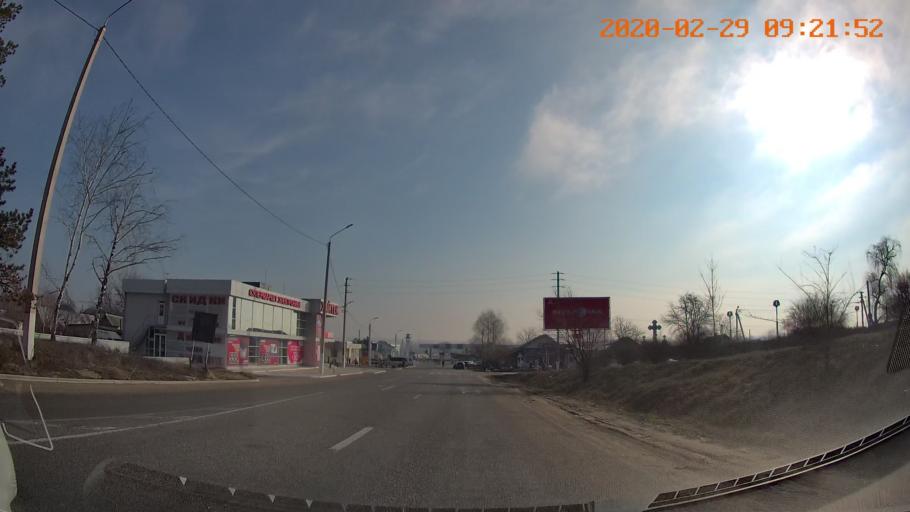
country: MD
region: Telenesti
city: Pervomaisc
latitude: 46.7380
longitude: 29.9641
